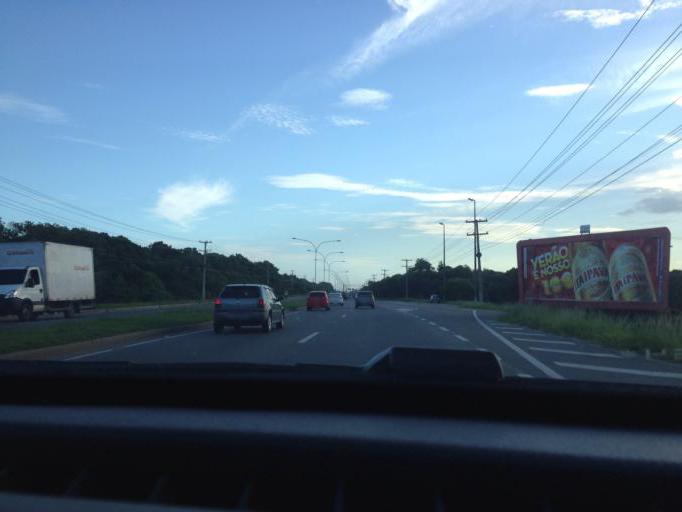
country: BR
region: Espirito Santo
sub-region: Vila Velha
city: Vila Velha
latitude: -20.4045
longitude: -40.3262
